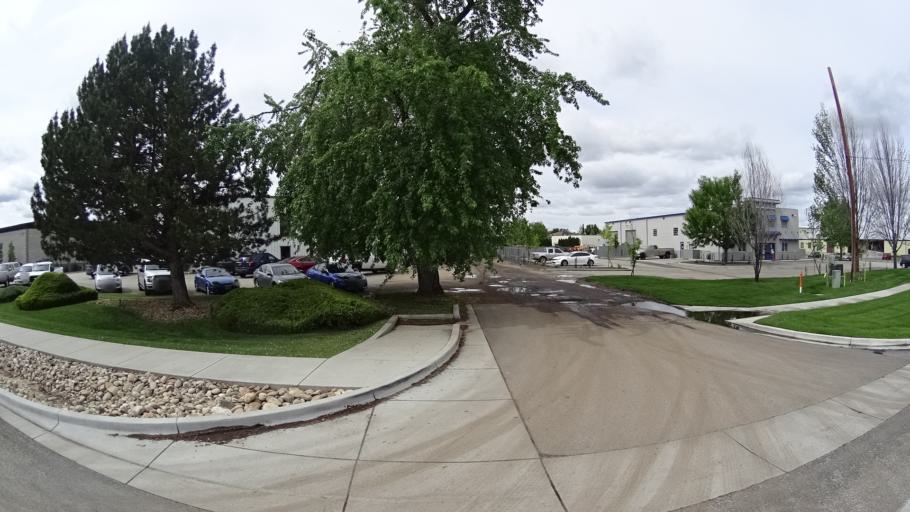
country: US
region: Idaho
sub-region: Ada County
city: Eagle
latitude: 43.6912
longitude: -116.3357
